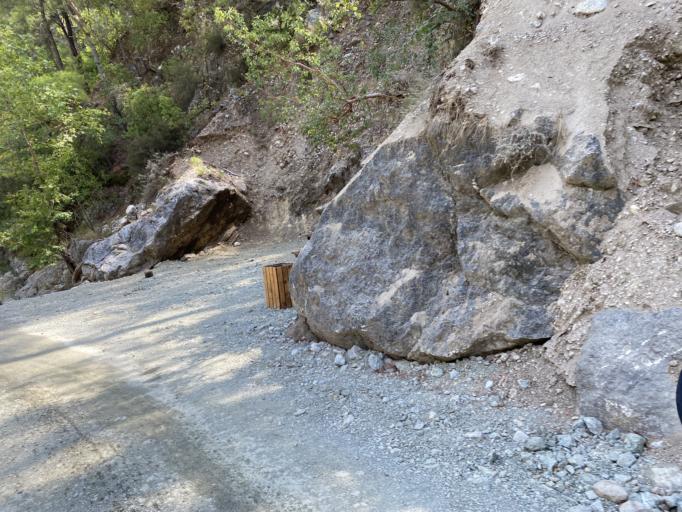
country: TR
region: Antalya
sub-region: Kemer
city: Goeynuek
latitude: 36.6810
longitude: 30.5274
